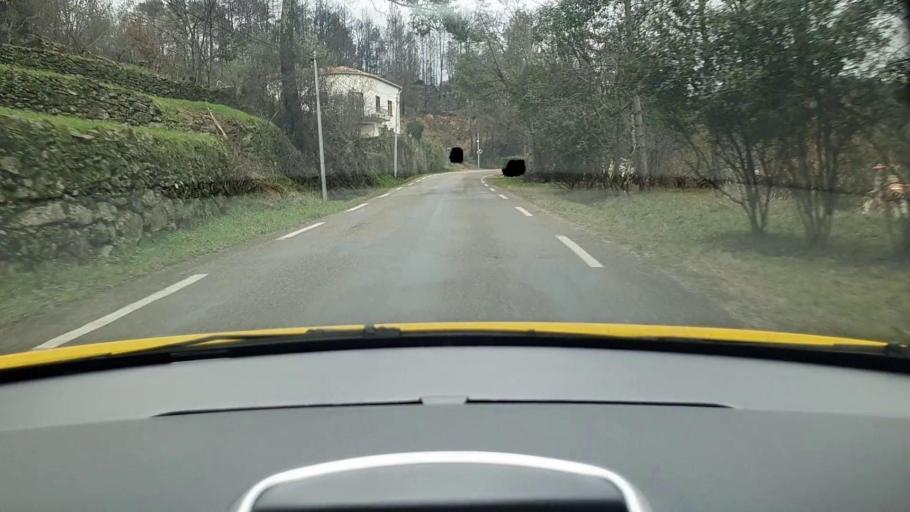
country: FR
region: Languedoc-Roussillon
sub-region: Departement du Gard
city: Besseges
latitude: 44.3083
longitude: 4.0918
